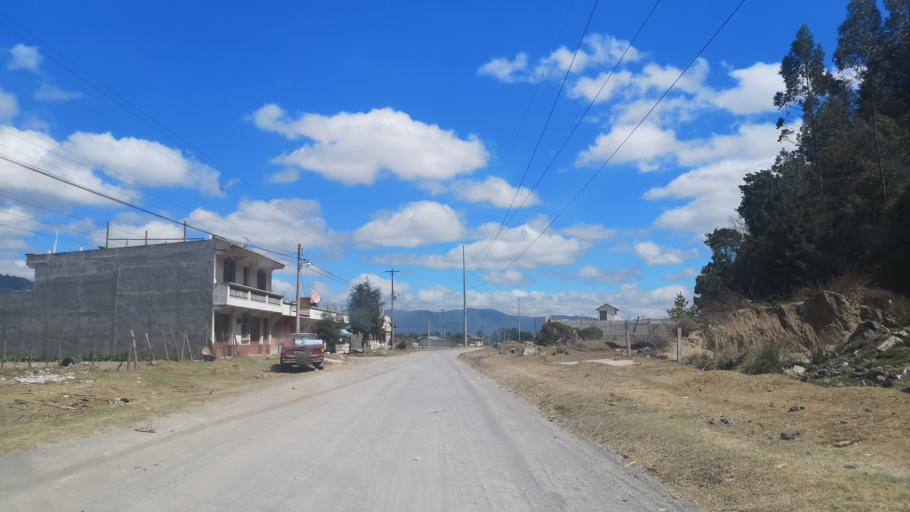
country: GT
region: Quetzaltenango
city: Almolonga
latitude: 14.7887
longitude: -91.5370
